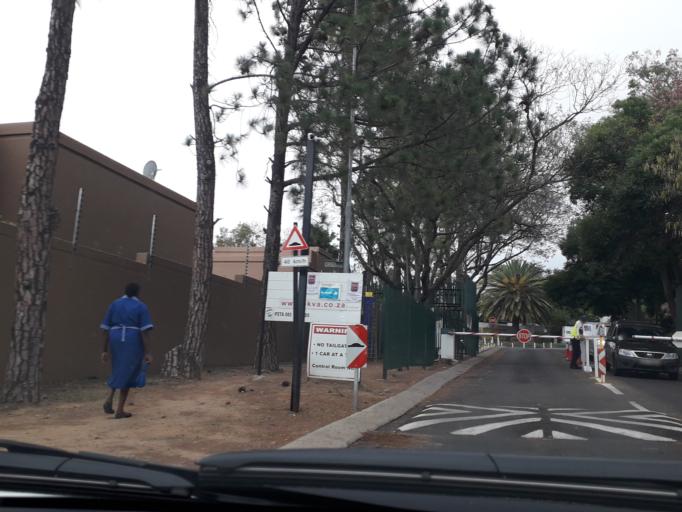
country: ZA
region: Gauteng
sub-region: City of Johannesburg Metropolitan Municipality
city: Johannesburg
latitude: -26.0883
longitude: 28.0371
